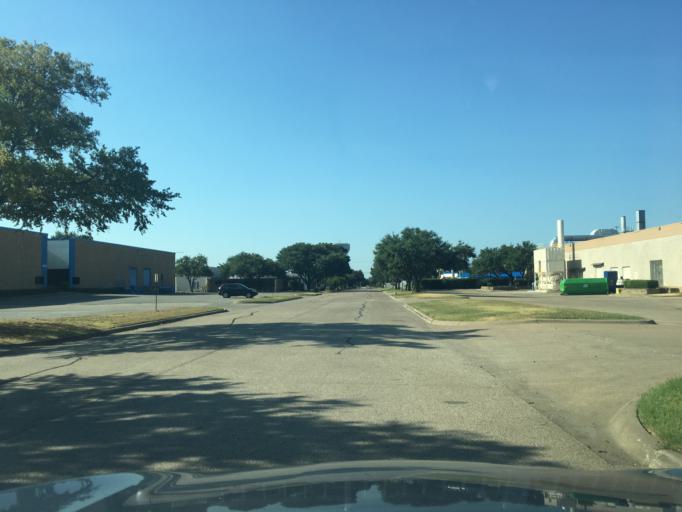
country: US
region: Texas
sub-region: Dallas County
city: Addison
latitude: 32.9617
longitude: -96.8468
